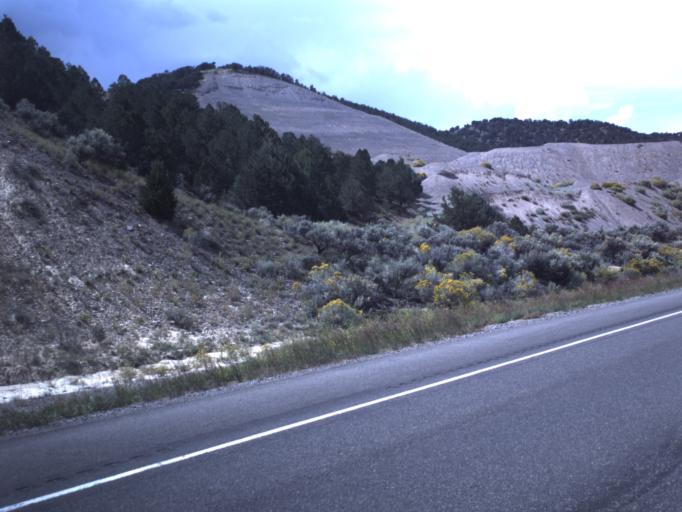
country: US
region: Utah
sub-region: Garfield County
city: Panguitch
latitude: 37.7630
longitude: -112.3855
